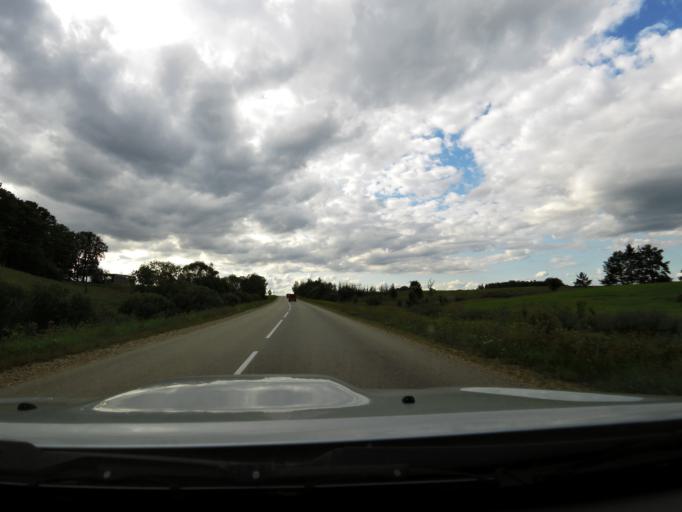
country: LV
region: Ilukste
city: Ilukste
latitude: 55.9787
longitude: 26.0092
